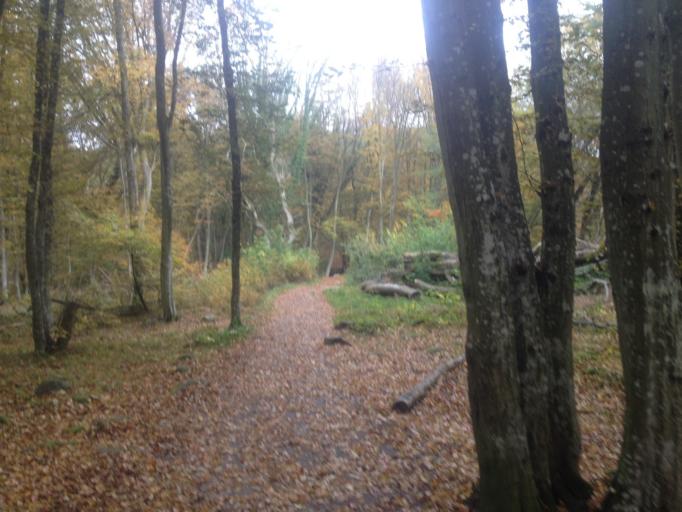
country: SE
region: Skane
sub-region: Simrishamns Kommun
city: Kivik
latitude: 55.6570
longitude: 14.2688
